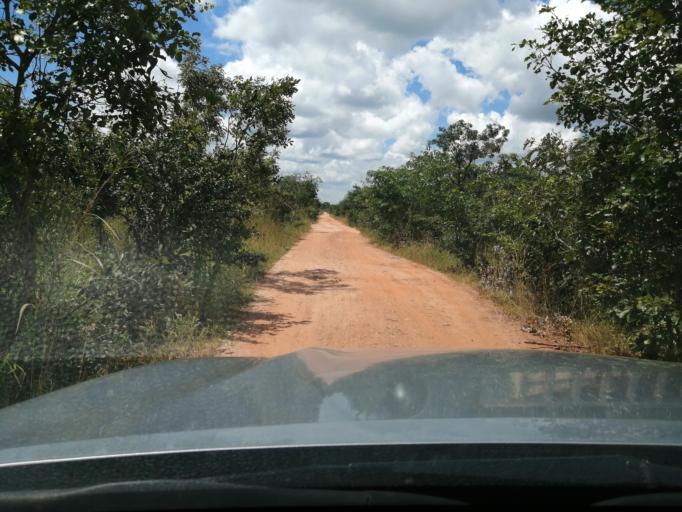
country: ZM
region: Lusaka
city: Lusaka
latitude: -15.1496
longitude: 27.9392
